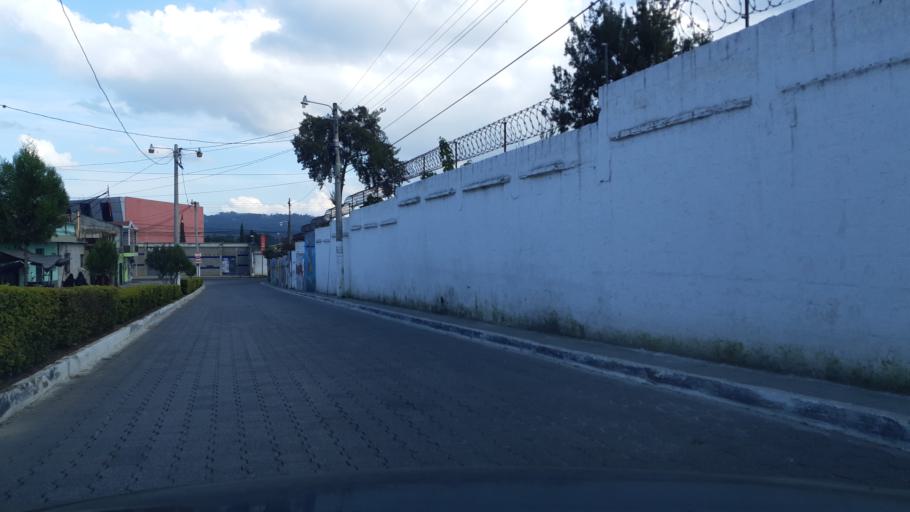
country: GT
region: Chimaltenango
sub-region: Municipio de Chimaltenango
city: Chimaltenango
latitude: 14.6565
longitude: -90.8157
